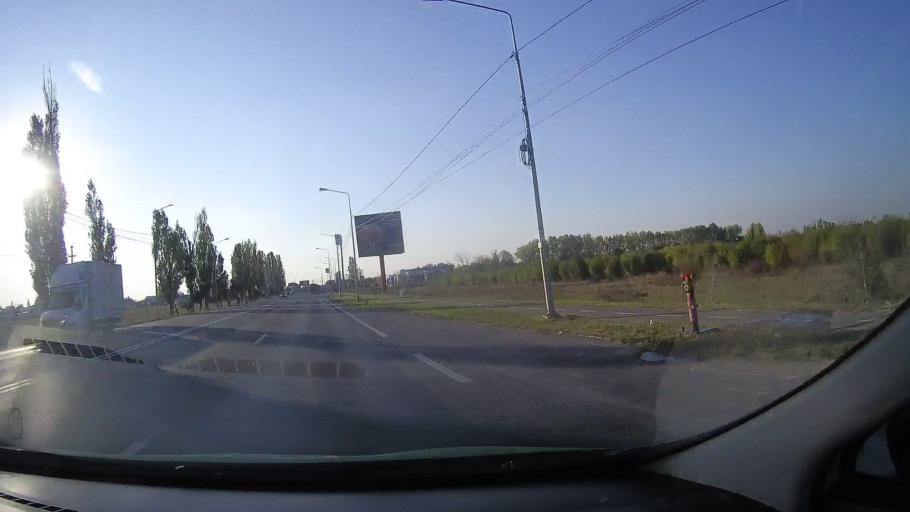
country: RO
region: Bihor
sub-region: Comuna Bors
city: Santion
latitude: 47.1005
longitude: 21.8475
